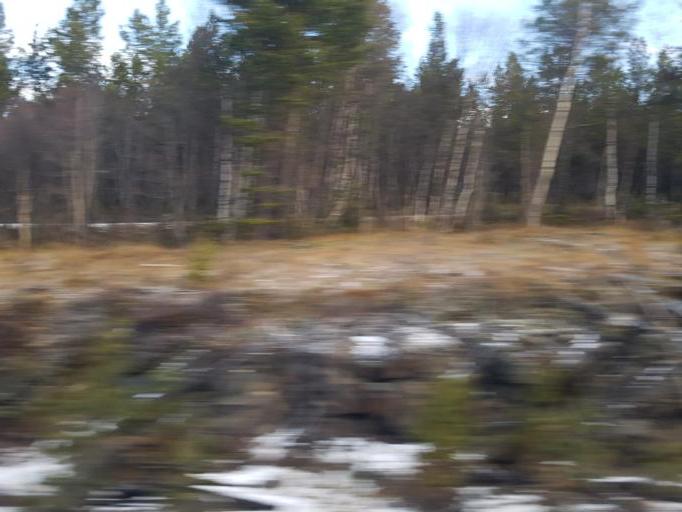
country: NO
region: Oppland
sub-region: Dovre
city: Dombas
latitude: 62.1080
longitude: 9.1635
